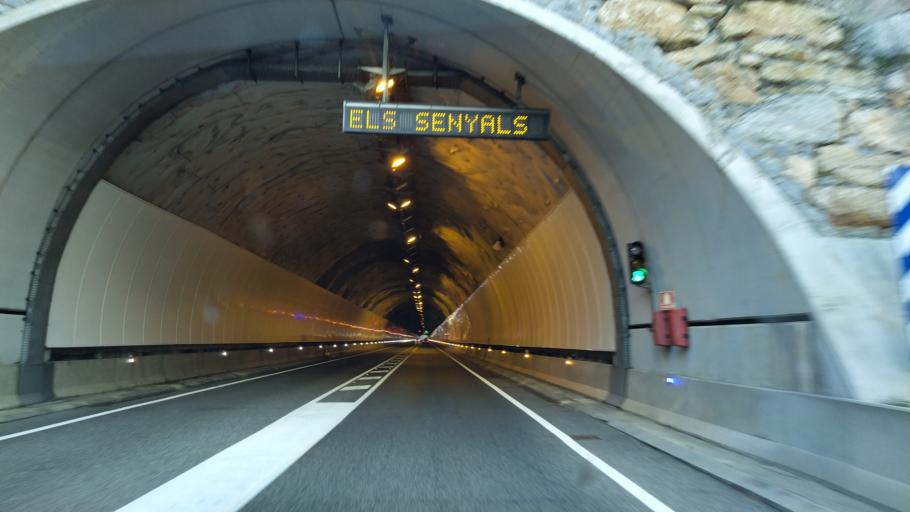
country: ES
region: Catalonia
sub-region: Provincia de Lleida
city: Coll de Nargo
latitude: 42.1363
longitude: 1.3094
